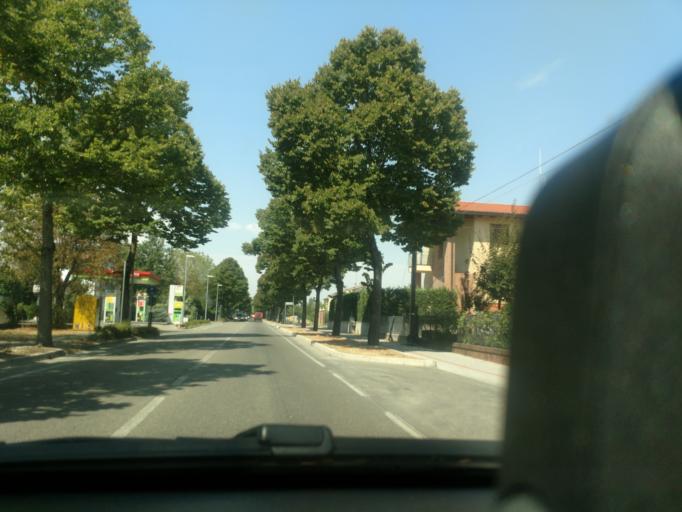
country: IT
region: Emilia-Romagna
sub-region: Provincia di Bologna
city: Castel Guelfo di Bologna
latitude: 44.4330
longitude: 11.6743
